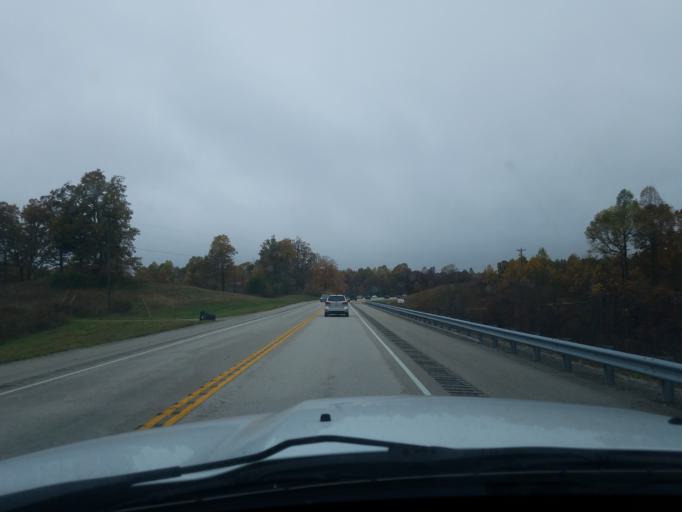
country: US
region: Kentucky
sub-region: Larue County
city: Hodgenville
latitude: 37.4652
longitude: -85.5763
